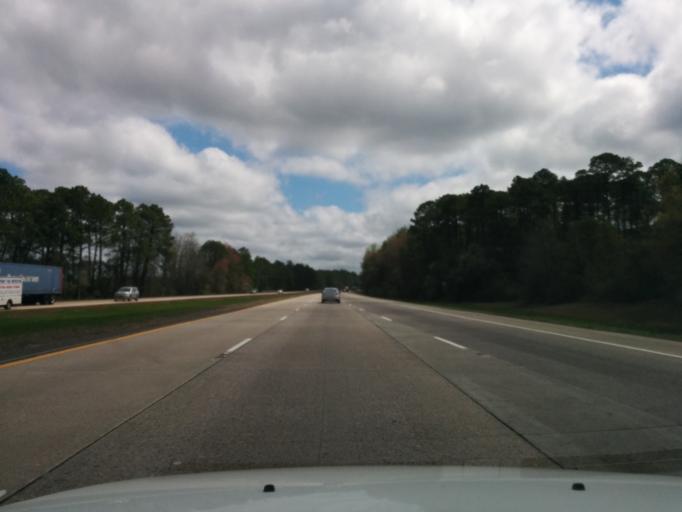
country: US
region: Georgia
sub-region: Chatham County
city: Bloomingdale
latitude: 32.1650
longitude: -81.4390
